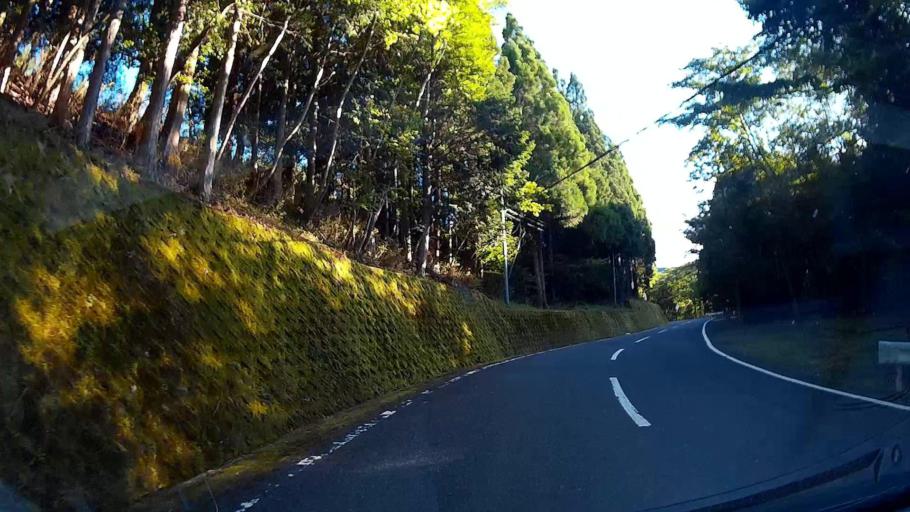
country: JP
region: Shizuoka
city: Shizuoka-shi
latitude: 35.1949
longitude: 138.2508
